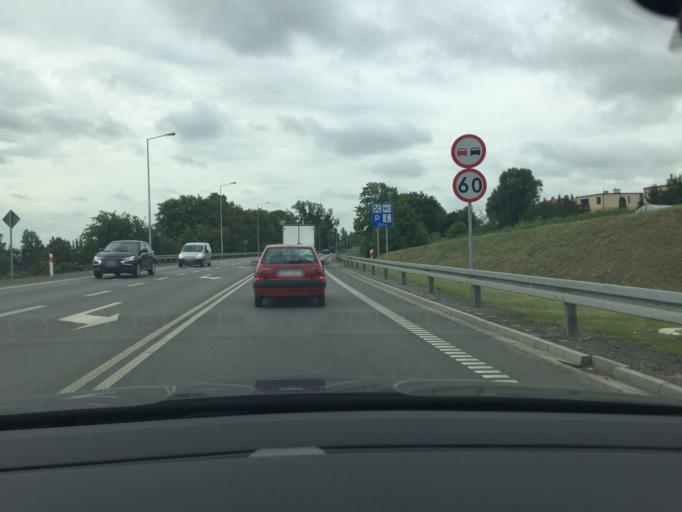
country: PL
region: Pomeranian Voivodeship
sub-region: Powiat tczewski
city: Tczew
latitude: 54.0730
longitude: 18.7761
